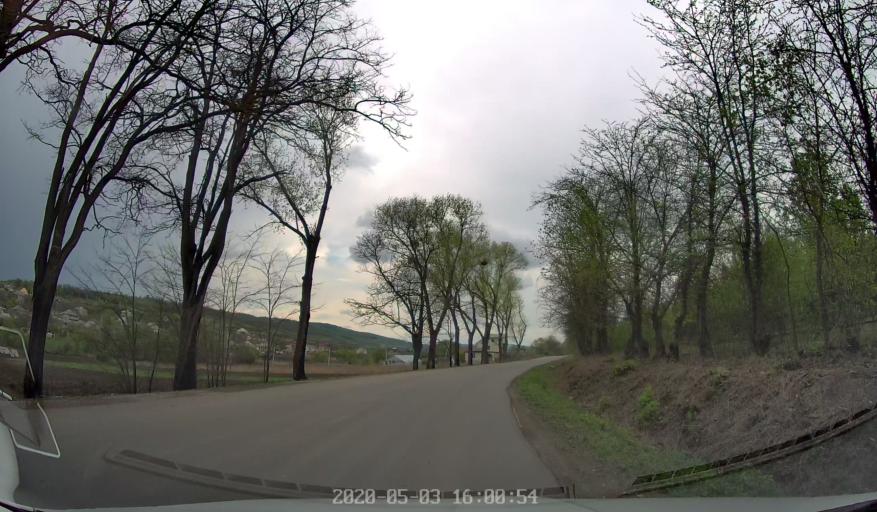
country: MD
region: Stinga Nistrului
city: Bucovat
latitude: 47.1622
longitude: 28.4150
